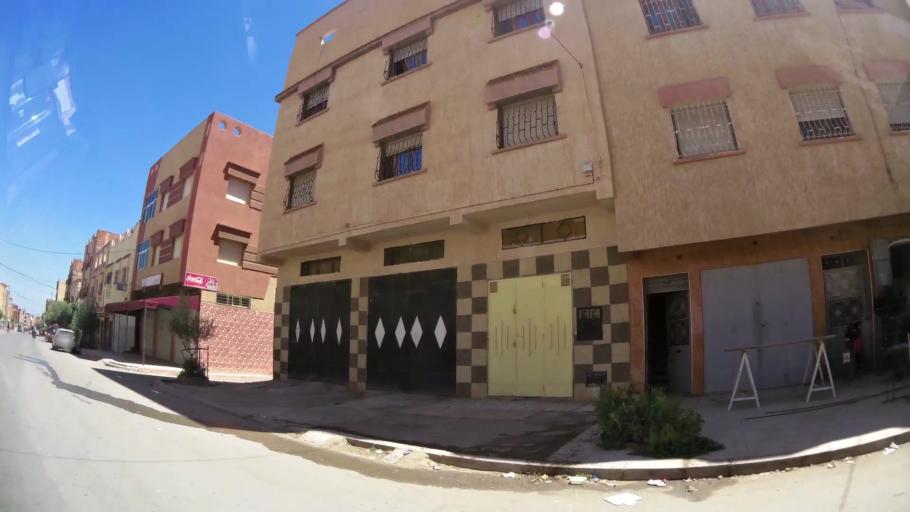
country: MA
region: Oriental
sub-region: Oujda-Angad
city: Oujda
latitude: 34.6637
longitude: -1.8815
